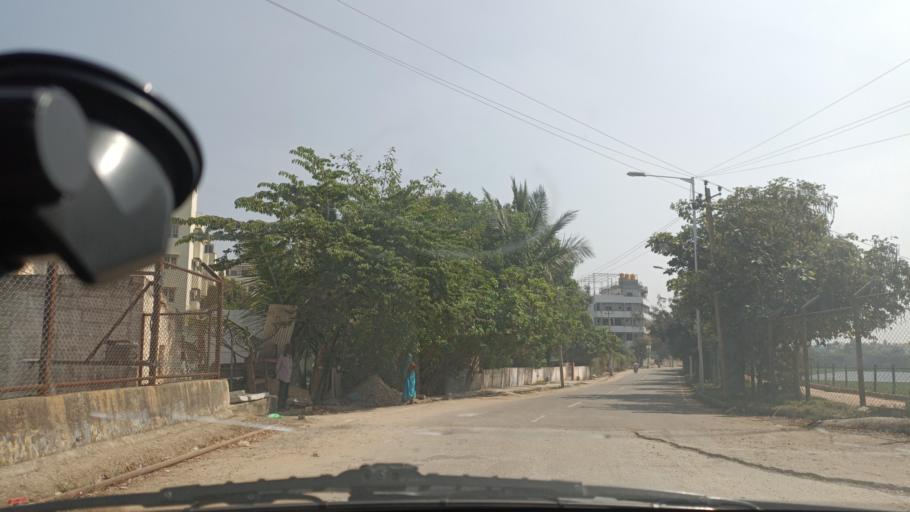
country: IN
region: Karnataka
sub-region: Bangalore Urban
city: Yelahanka
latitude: 13.1177
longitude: 77.6163
